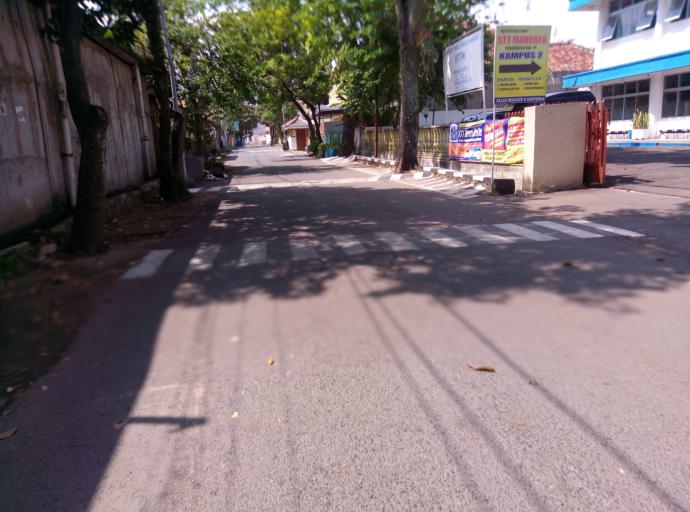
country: ID
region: West Java
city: Bandung
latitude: -6.9435
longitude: 107.6437
